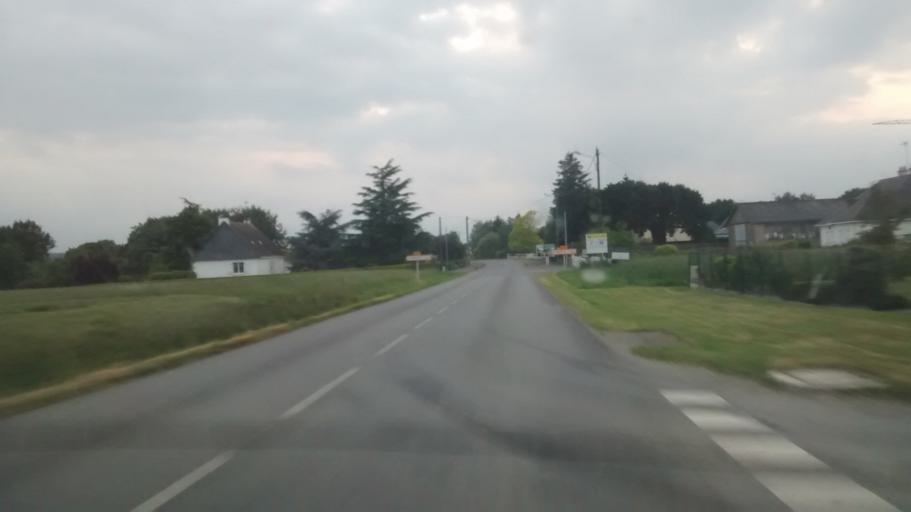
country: FR
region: Brittany
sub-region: Departement du Morbihan
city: Saint-Martin-sur-Oust
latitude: 47.7449
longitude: -2.2444
